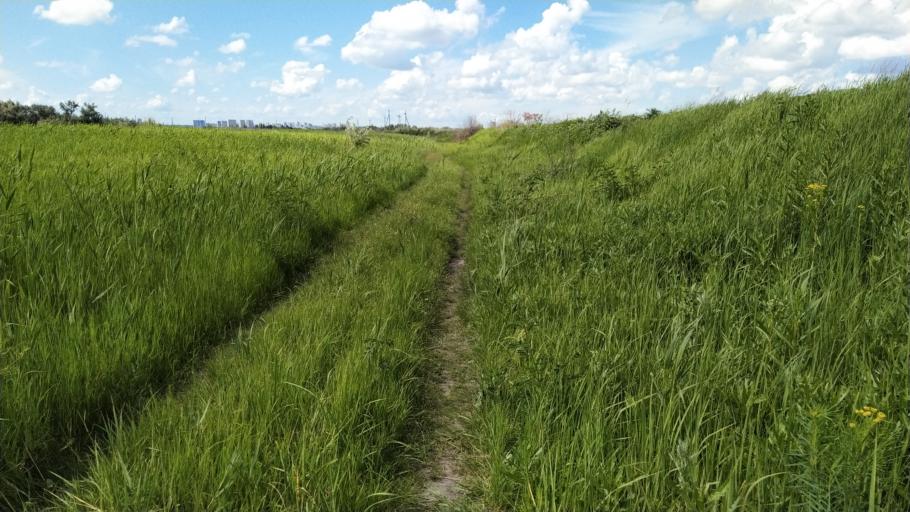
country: RU
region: Rostov
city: Bataysk
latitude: 47.1389
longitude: 39.6695
